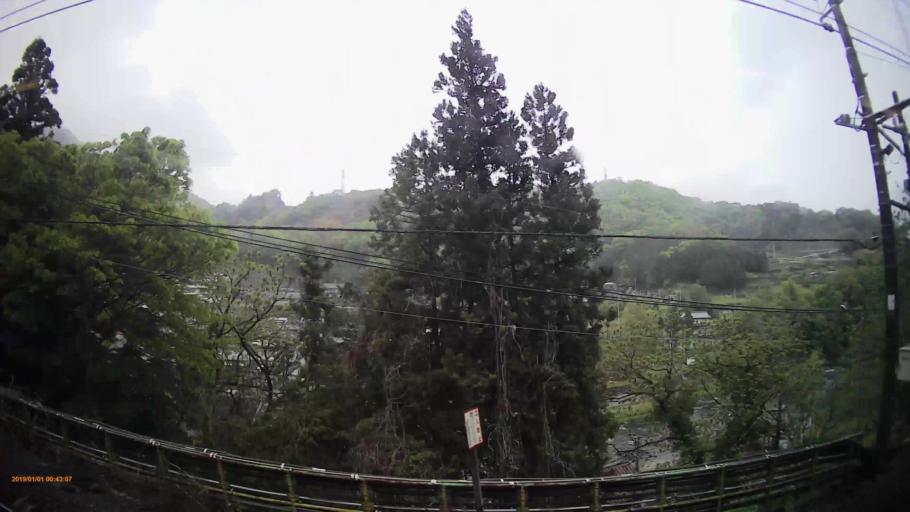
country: JP
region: Yamanashi
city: Otsuki
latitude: 35.6131
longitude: 138.9577
